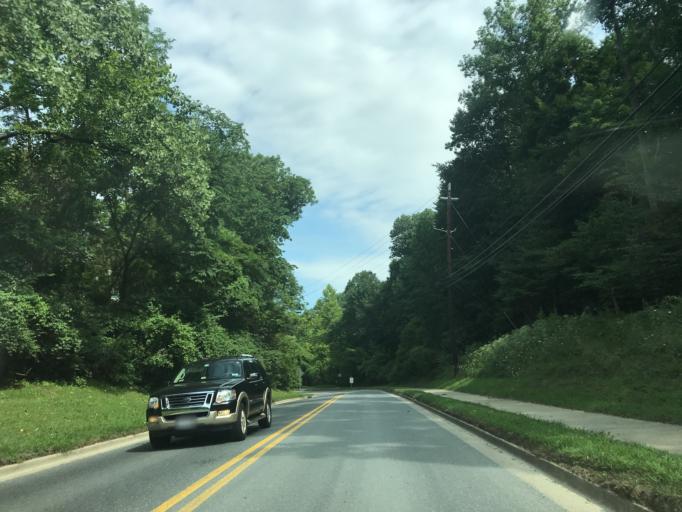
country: US
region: Maryland
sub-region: Montgomery County
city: Cabin John
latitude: 38.9891
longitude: -77.1605
